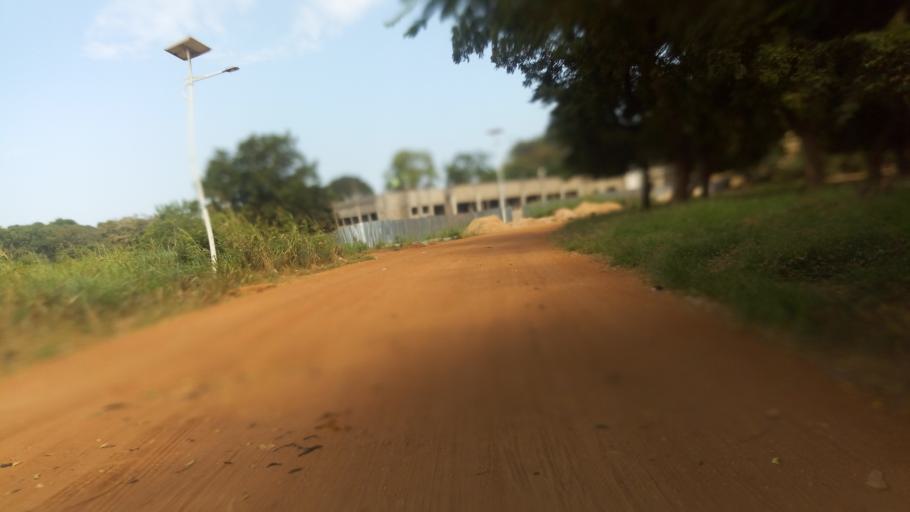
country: TG
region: Maritime
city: Lome
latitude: 6.1767
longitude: 1.2143
